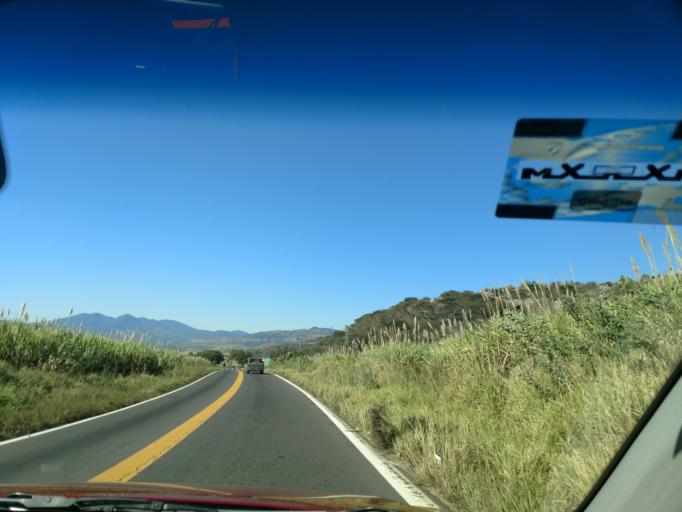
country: MX
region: Nayarit
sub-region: Ahuacatlan
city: Ahuacatlan
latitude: 21.1099
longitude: -104.5878
